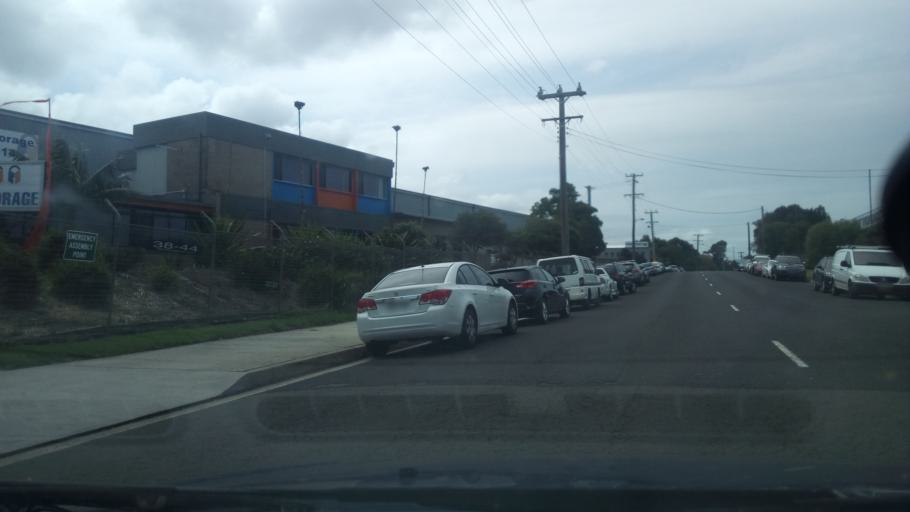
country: AU
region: New South Wales
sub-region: Wollongong
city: Fairy Meadow
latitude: -34.4002
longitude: 150.8955
